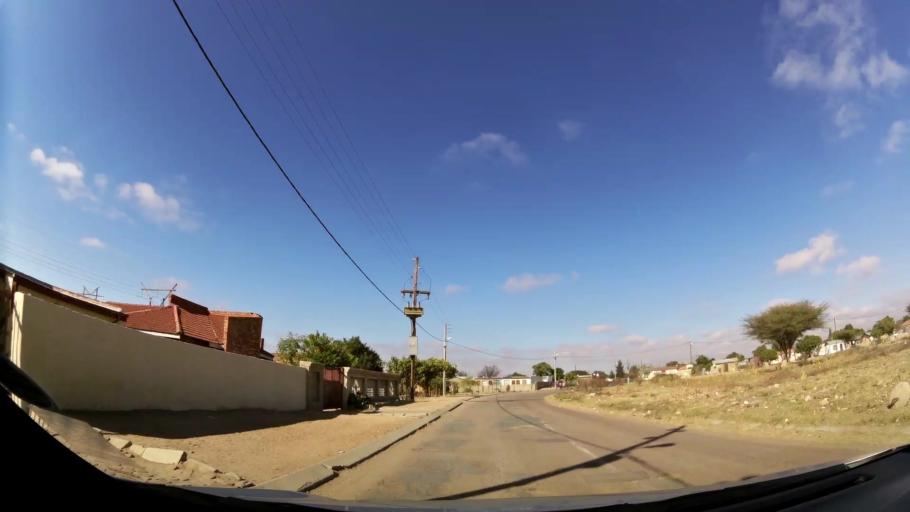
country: ZA
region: Limpopo
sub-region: Capricorn District Municipality
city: Polokwane
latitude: -23.8491
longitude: 29.4055
